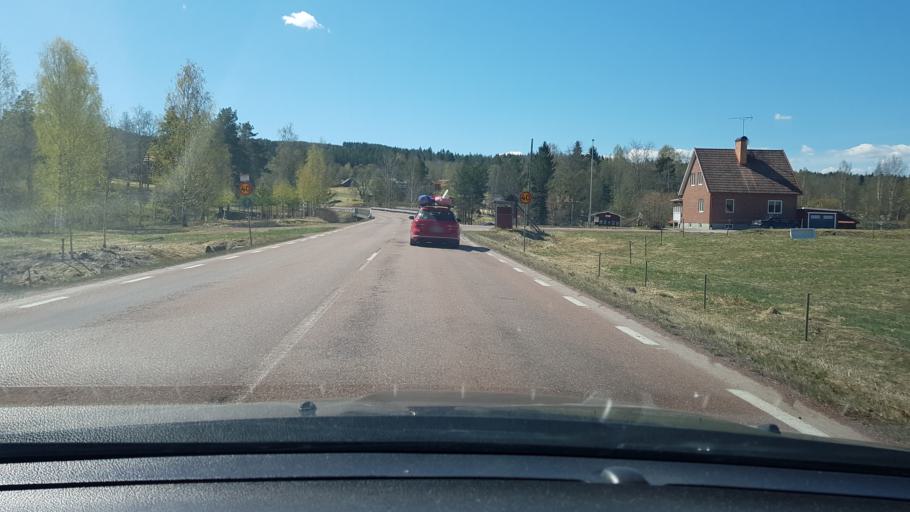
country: SE
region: Dalarna
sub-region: Alvdalens Kommun
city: AElvdalen
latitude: 61.1212
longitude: 14.1719
